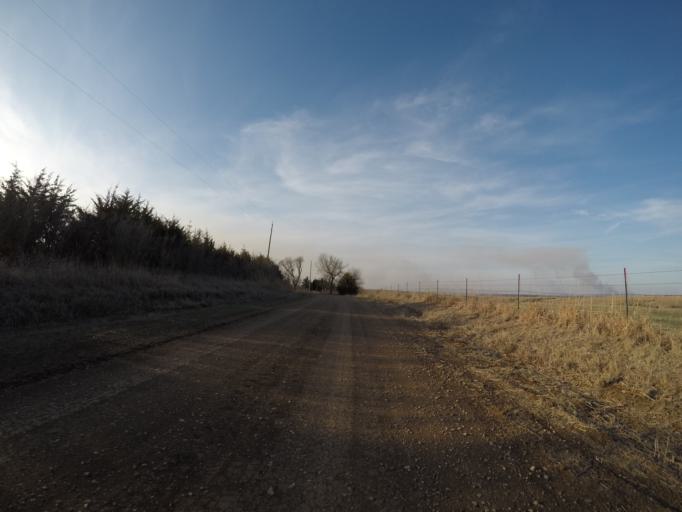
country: US
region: Kansas
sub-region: Riley County
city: Manhattan
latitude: 39.2531
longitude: -96.6585
